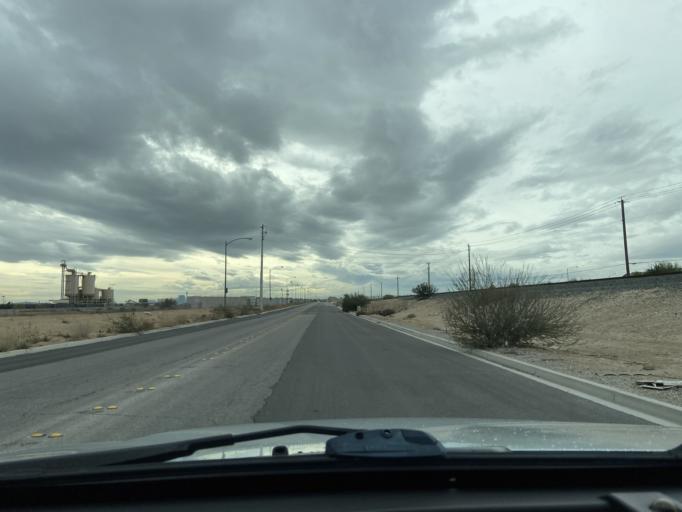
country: US
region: Nevada
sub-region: Clark County
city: Nellis Air Force Base
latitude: 36.2554
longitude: -115.0908
